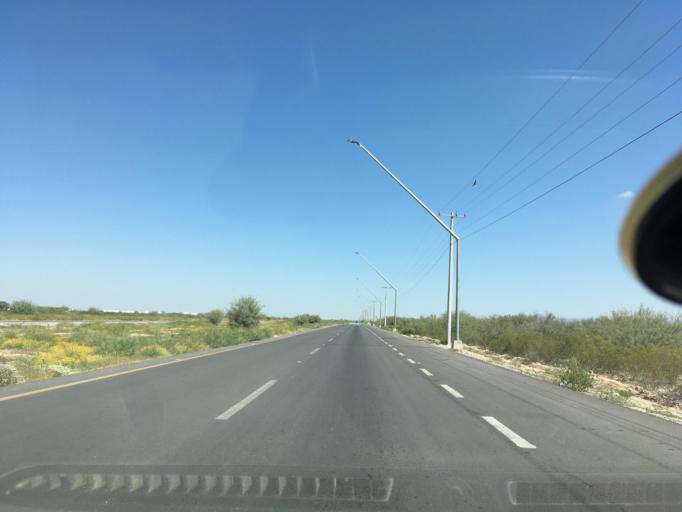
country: MX
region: Coahuila
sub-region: Torreon
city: Fraccionamiento la Noria
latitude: 25.4666
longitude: -103.3225
